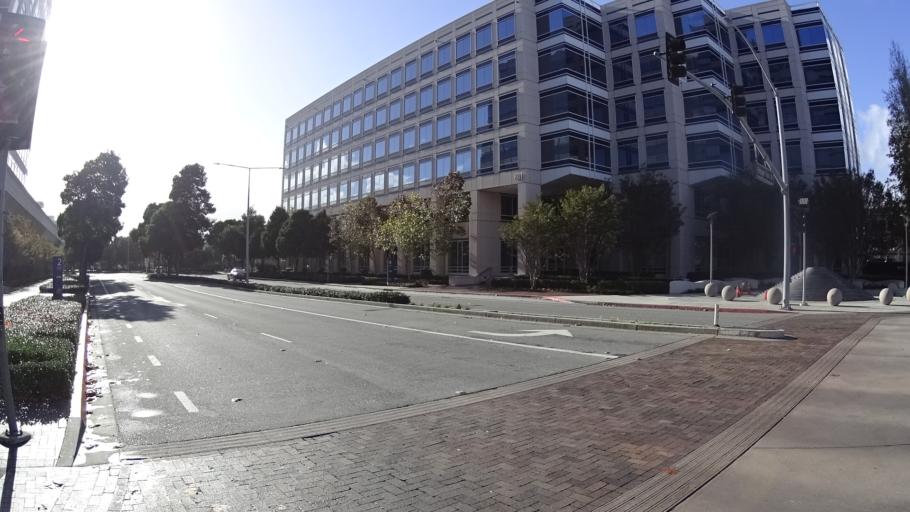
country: US
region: California
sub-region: San Mateo County
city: Foster City
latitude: 37.5590
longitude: -122.2774
